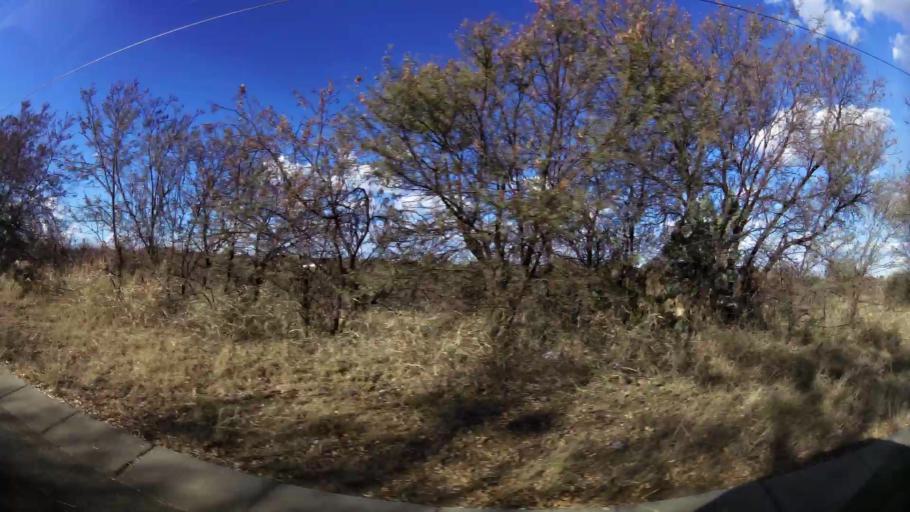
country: ZA
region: North-West
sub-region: Dr Kenneth Kaunda District Municipality
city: Klerksdorp
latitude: -26.8355
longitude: 26.6622
